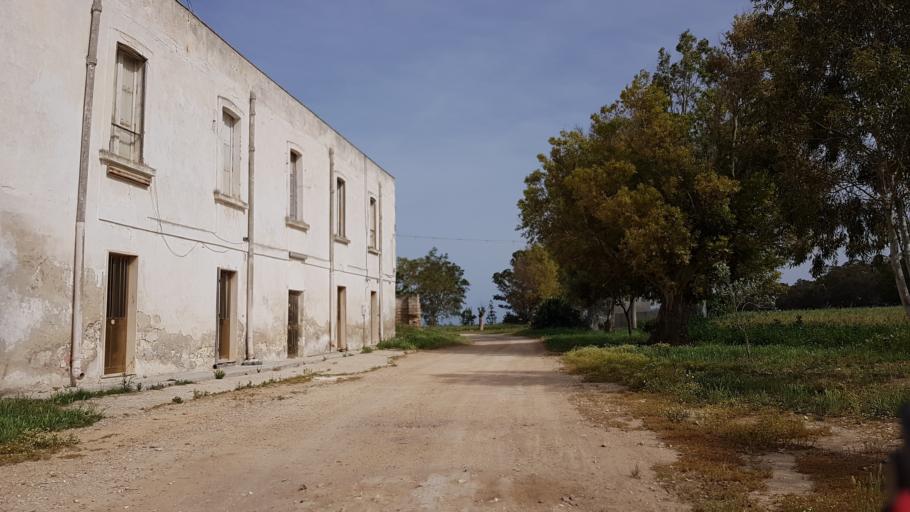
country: IT
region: Apulia
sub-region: Provincia di Brindisi
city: La Rosa
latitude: 40.5955
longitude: 18.0309
